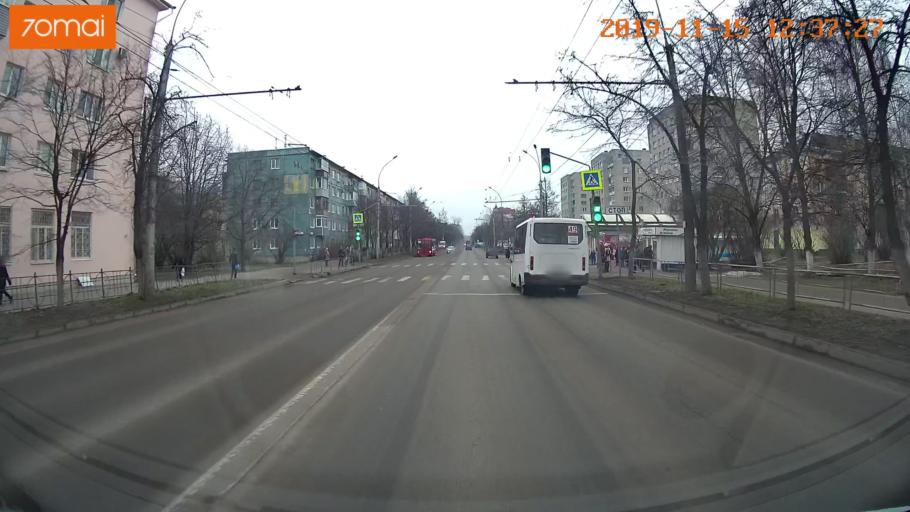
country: RU
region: Vologda
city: Vologda
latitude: 59.2090
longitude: 39.8990
